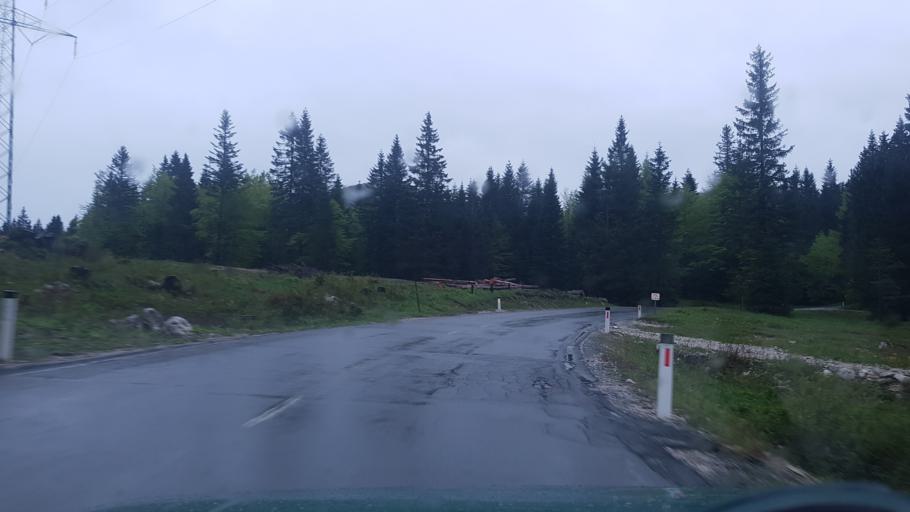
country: SI
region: Bohinj
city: Bohinjska Bistrica
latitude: 46.2449
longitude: 14.0069
